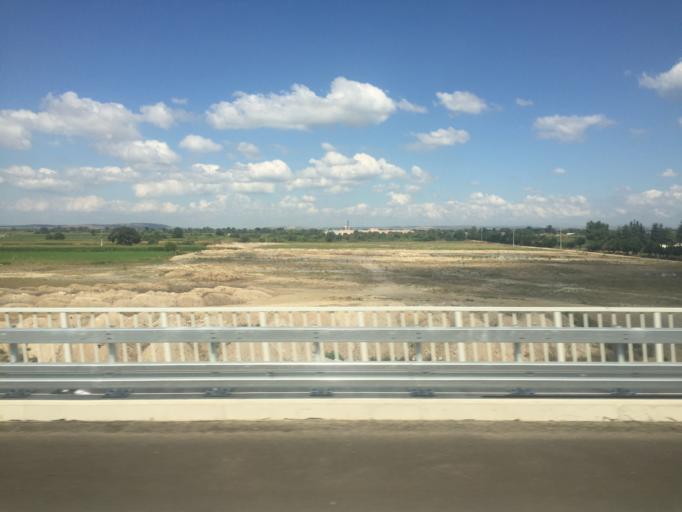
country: TR
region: Balikesir
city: Gobel
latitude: 40.0685
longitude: 28.2489
